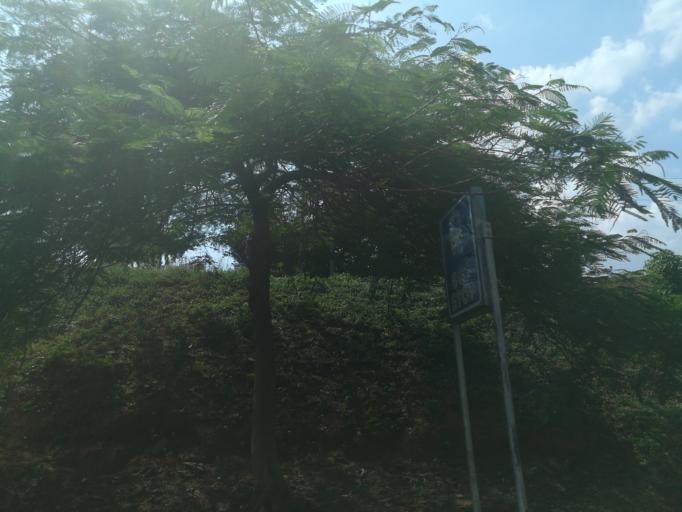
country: NG
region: Abuja Federal Capital Territory
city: Abuja
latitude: 9.0641
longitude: 7.4522
